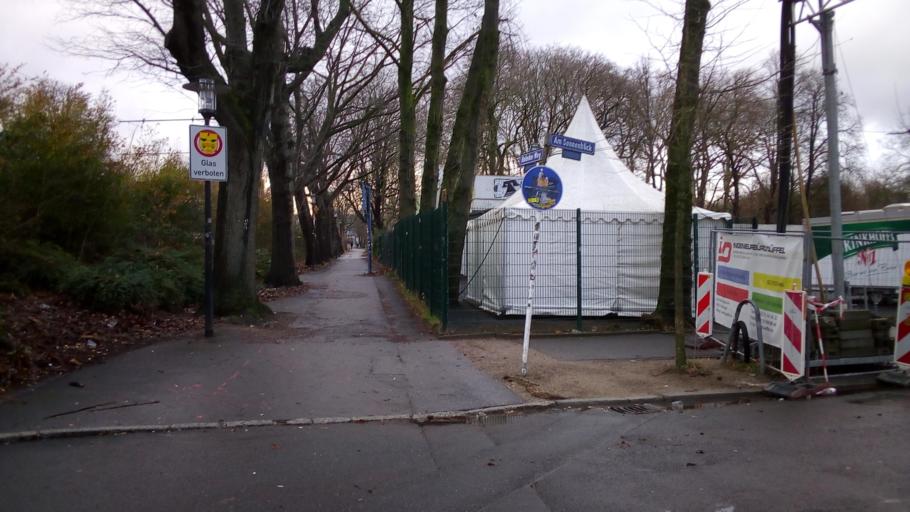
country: DE
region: North Rhine-Westphalia
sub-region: Regierungsbezirk Arnsberg
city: Dortmund
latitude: 51.4922
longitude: 7.4569
